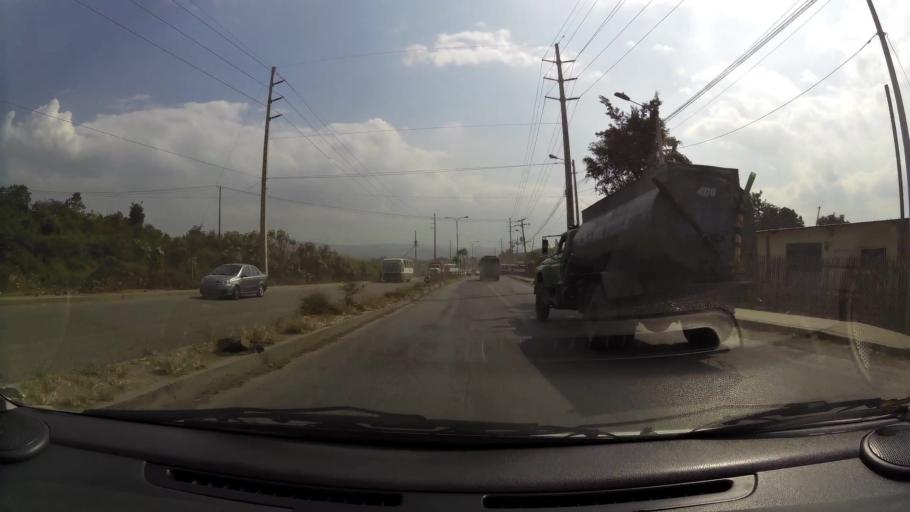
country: EC
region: Guayas
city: Santa Lucia
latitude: -2.1208
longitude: -79.9774
